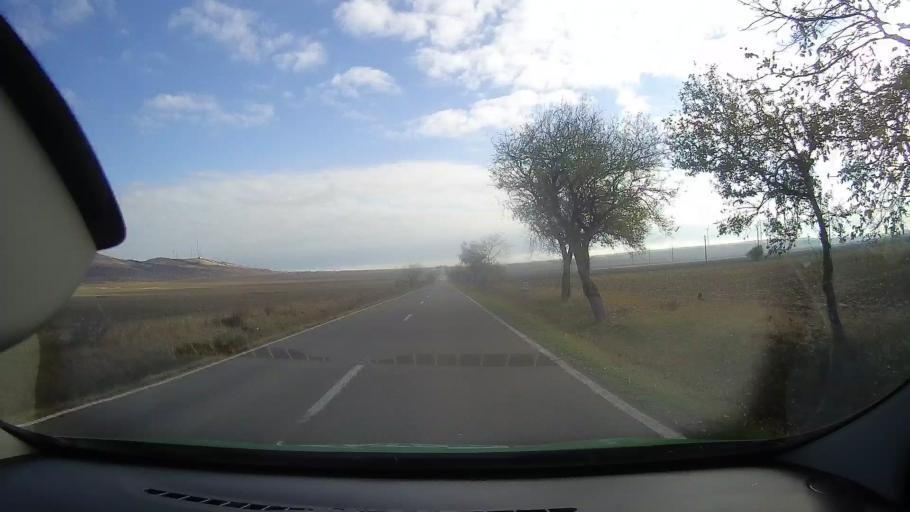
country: RO
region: Tulcea
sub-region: Comuna Bestepe
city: Bestepe
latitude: 45.0779
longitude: 29.0462
